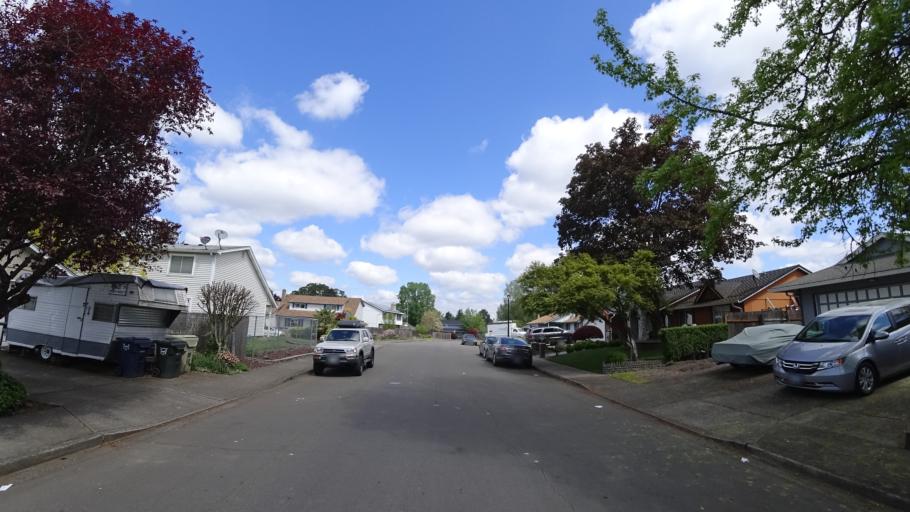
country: US
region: Oregon
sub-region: Washington County
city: Aloha
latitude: 45.5022
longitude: -122.8957
